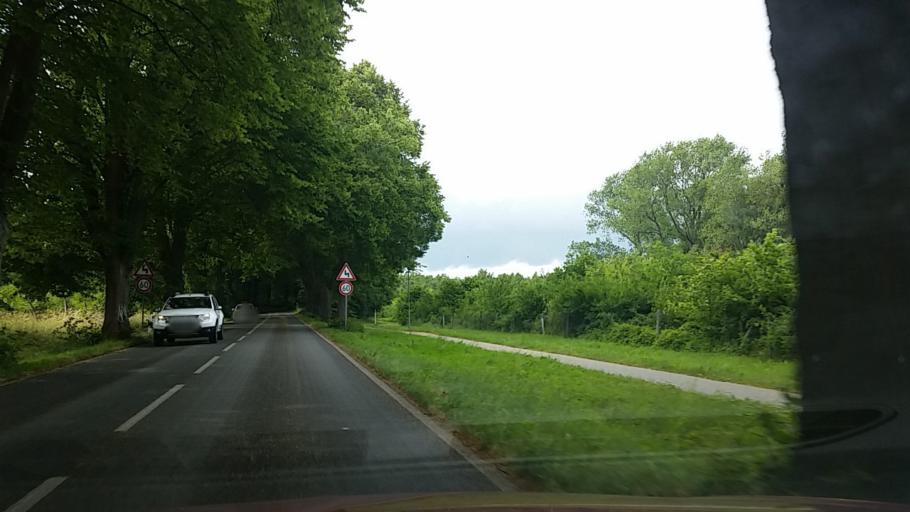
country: DE
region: Mecklenburg-Vorpommern
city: Ostseebad Kuhlungsborn
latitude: 54.1369
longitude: 11.7815
